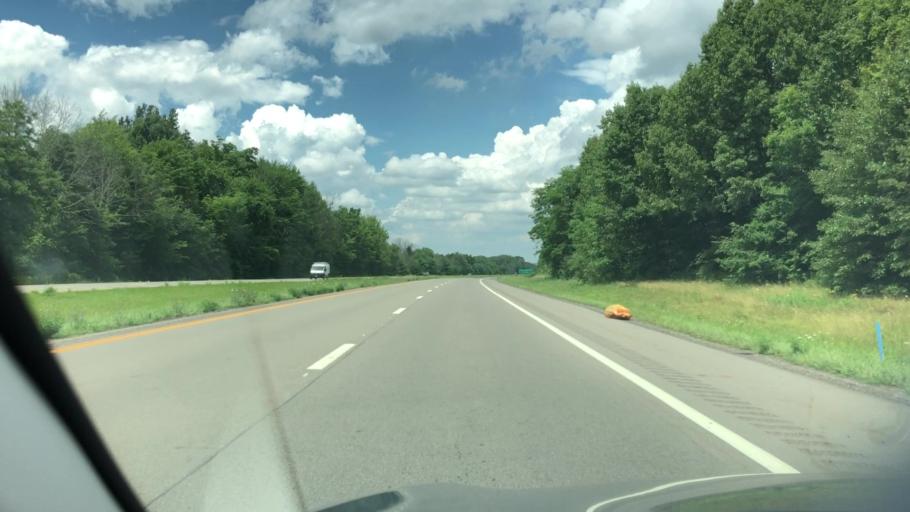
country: US
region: Ohio
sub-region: Stark County
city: Massillon
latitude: 40.8289
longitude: -81.5431
